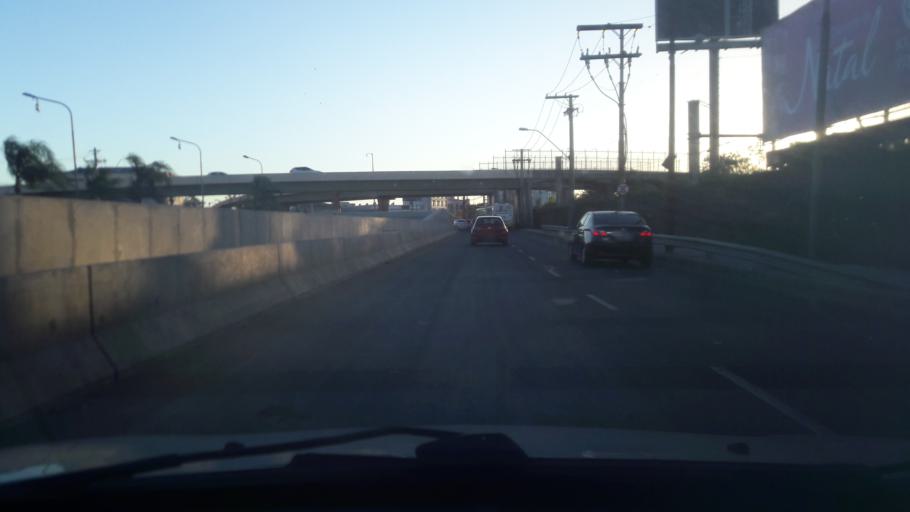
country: BR
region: Rio Grande do Sul
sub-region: Porto Alegre
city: Porto Alegre
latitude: -29.9951
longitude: -51.1887
